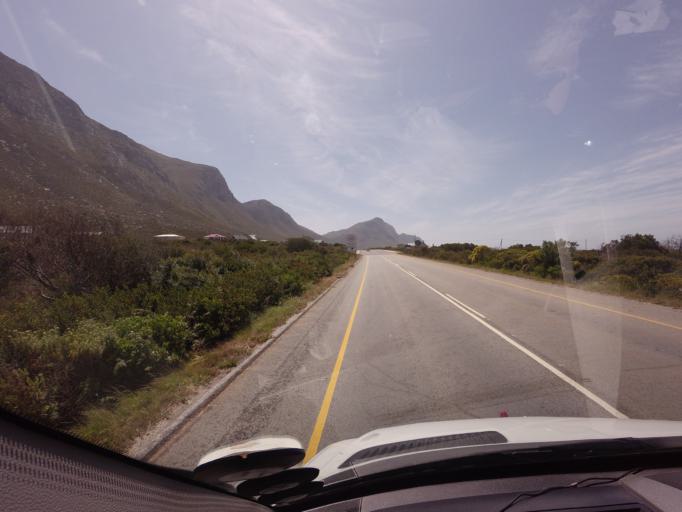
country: ZA
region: Western Cape
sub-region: Overberg District Municipality
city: Grabouw
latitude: -34.3584
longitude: 18.8908
